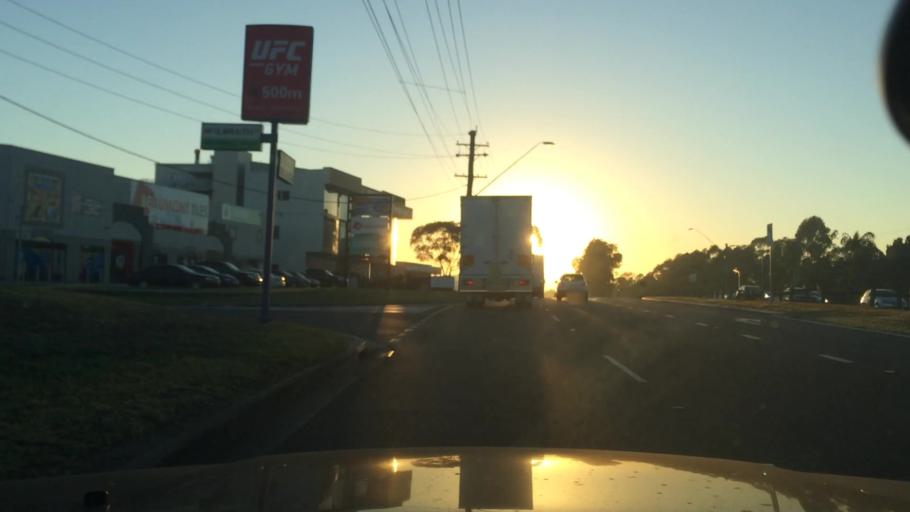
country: AU
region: New South Wales
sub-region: Fairfield
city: Horsley Park
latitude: -33.8525
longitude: 150.8909
